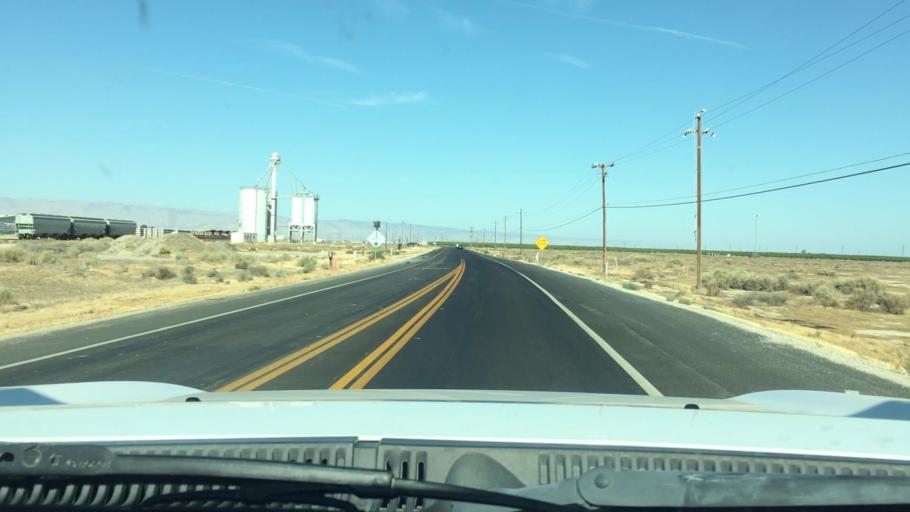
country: US
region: California
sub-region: Kern County
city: Buttonwillow
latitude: 35.3996
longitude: -119.4024
